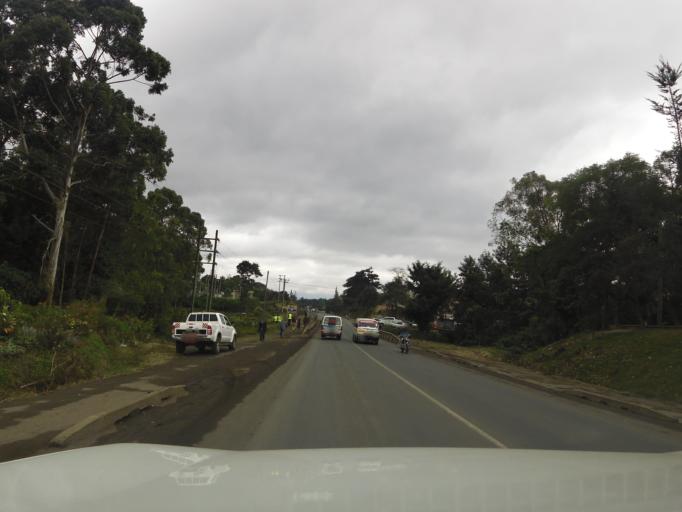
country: TZ
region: Arusha
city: Arusha
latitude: -3.3639
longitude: 36.7030
